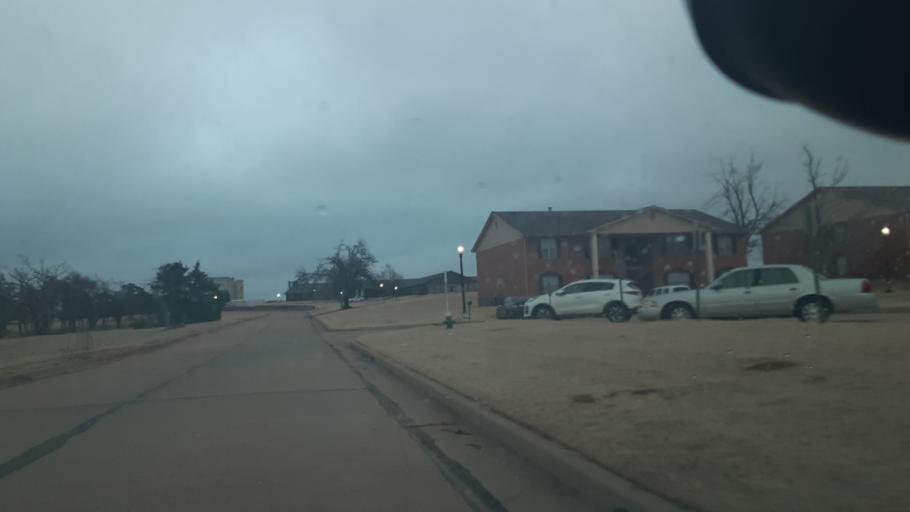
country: US
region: Oklahoma
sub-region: Logan County
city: Guthrie
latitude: 35.8744
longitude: -97.4003
